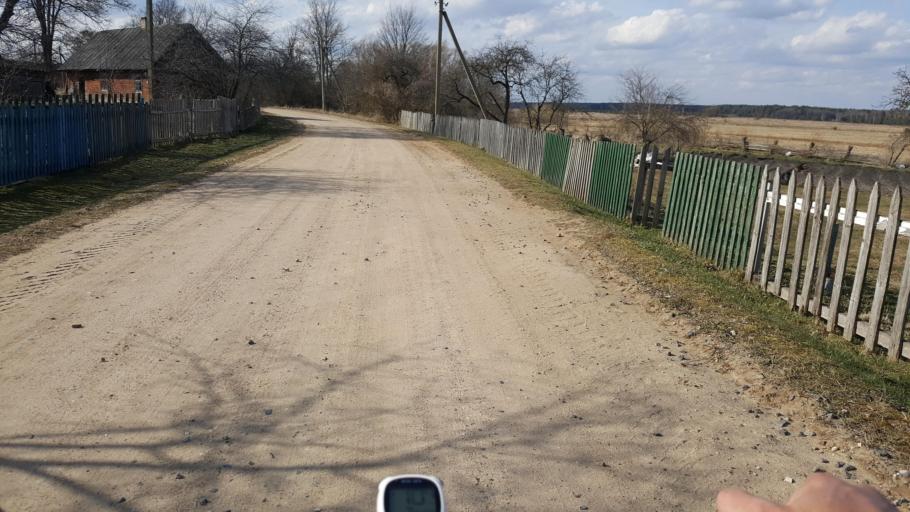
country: BY
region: Brest
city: Kamyanyets
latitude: 52.4012
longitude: 23.9578
